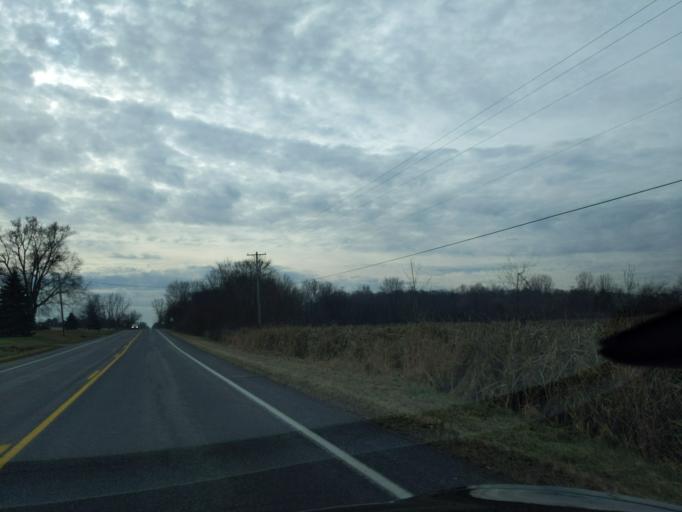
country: US
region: Michigan
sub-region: Ingham County
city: Holt
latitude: 42.5929
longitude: -84.5230
